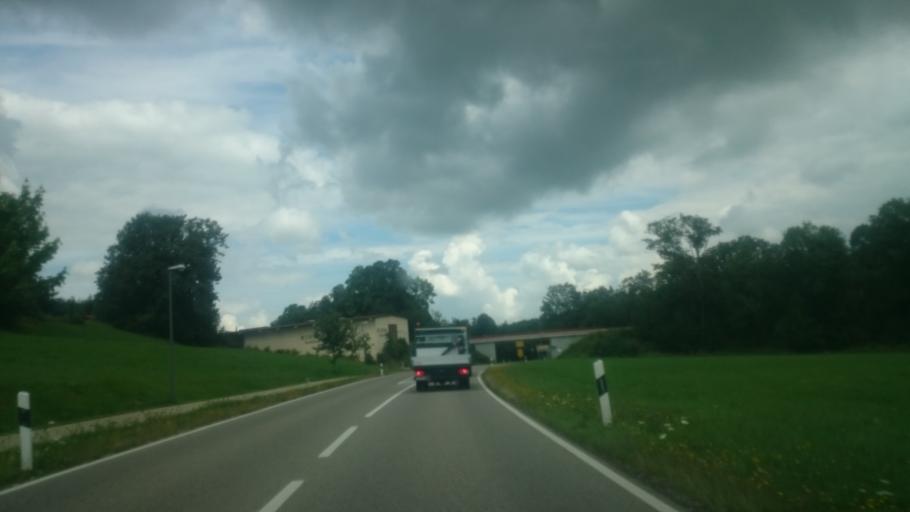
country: DE
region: Bavaria
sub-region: Swabia
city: Gunzach
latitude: 47.8177
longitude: 10.4421
